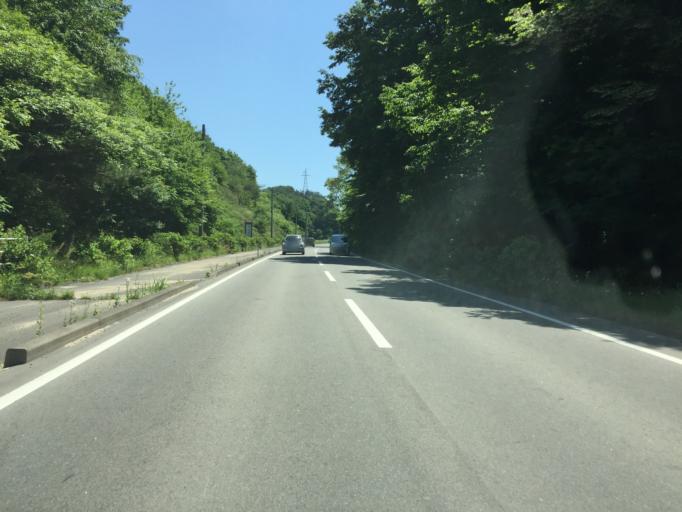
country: JP
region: Fukushima
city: Motomiya
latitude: 37.5345
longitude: 140.4187
